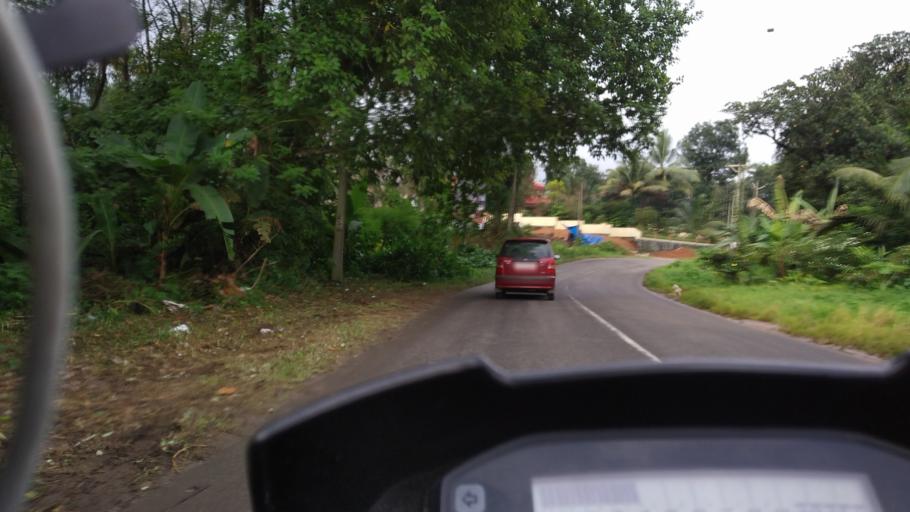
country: IN
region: Kerala
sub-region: Idukki
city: Kuttampuzha
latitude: 10.0507
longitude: 76.7543
